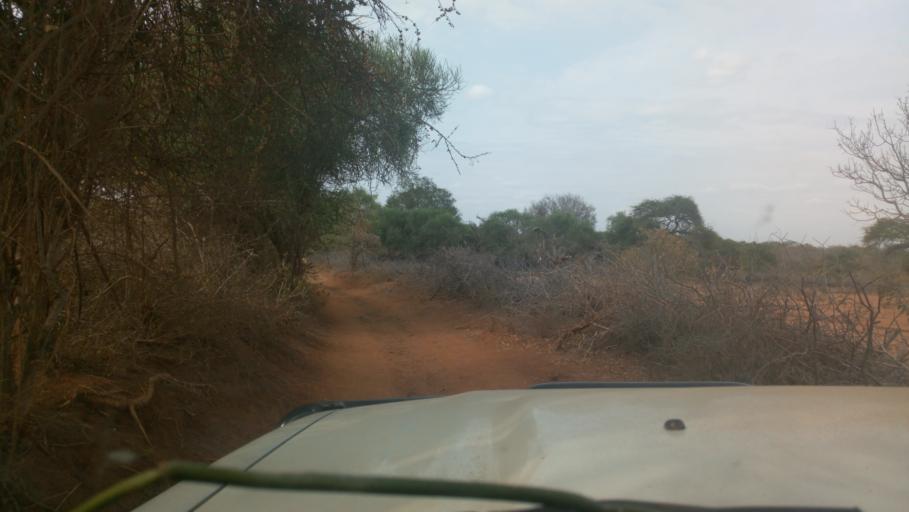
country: KE
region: Kitui
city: Kitui
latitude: -1.6338
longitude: 37.9265
